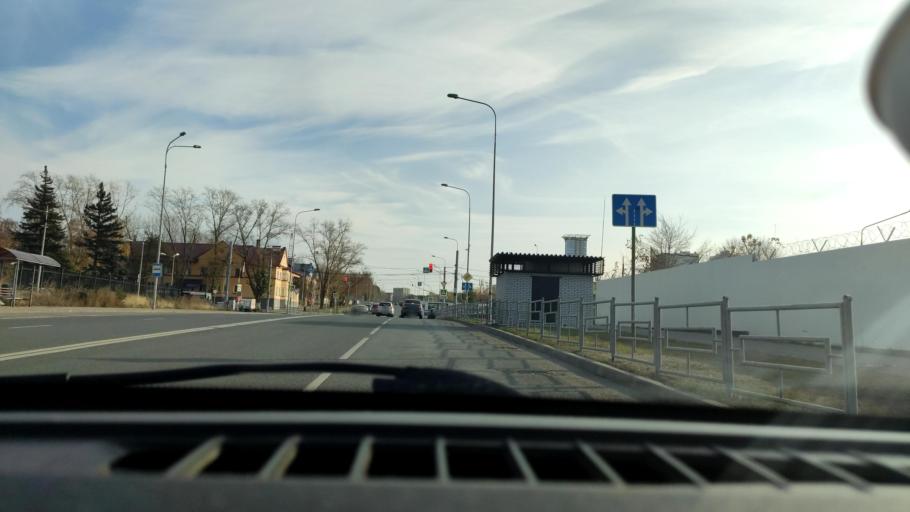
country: RU
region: Samara
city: Samara
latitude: 53.2102
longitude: 50.1510
